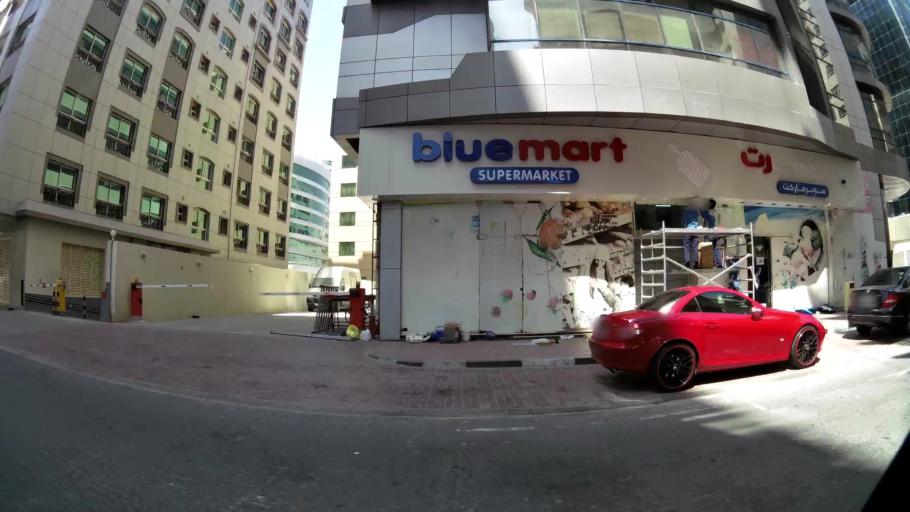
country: AE
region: Dubai
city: Dubai
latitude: 25.1106
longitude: 55.2027
